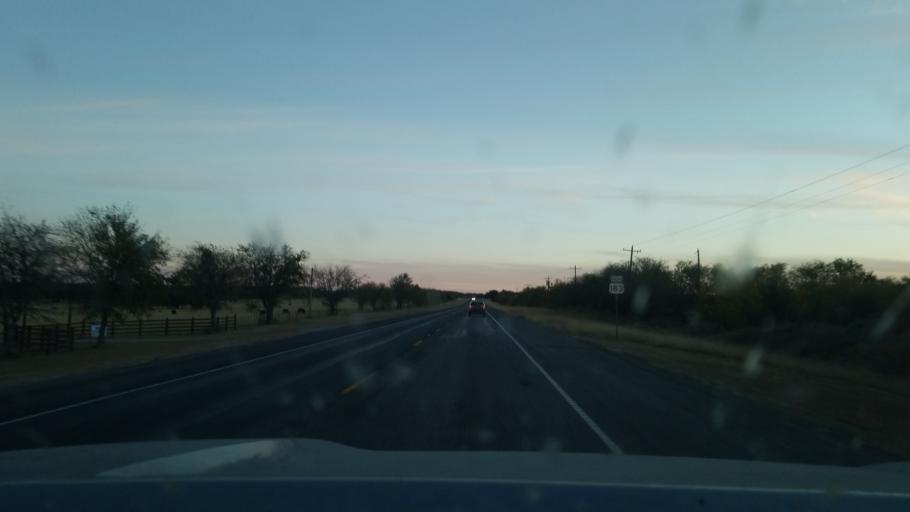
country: US
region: Texas
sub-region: Stephens County
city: Breckenridge
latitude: 32.5912
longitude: -98.8984
